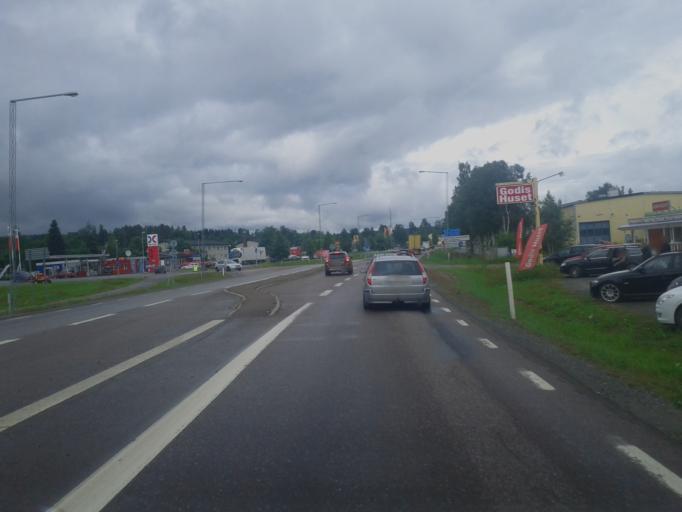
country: SE
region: Vaesternorrland
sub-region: Haernoesands Kommun
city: Haernoesand
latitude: 62.6729
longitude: 17.8400
